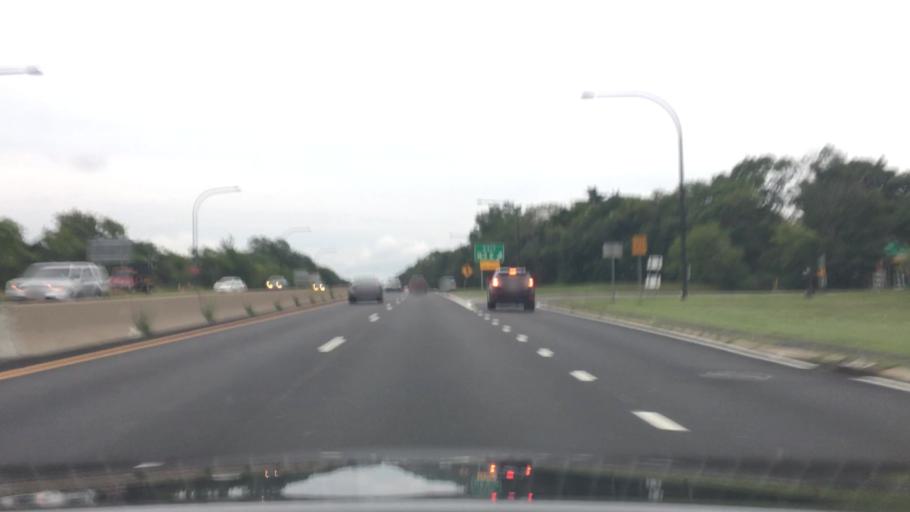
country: US
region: New York
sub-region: Nassau County
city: Levittown
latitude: 40.7232
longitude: -73.5373
